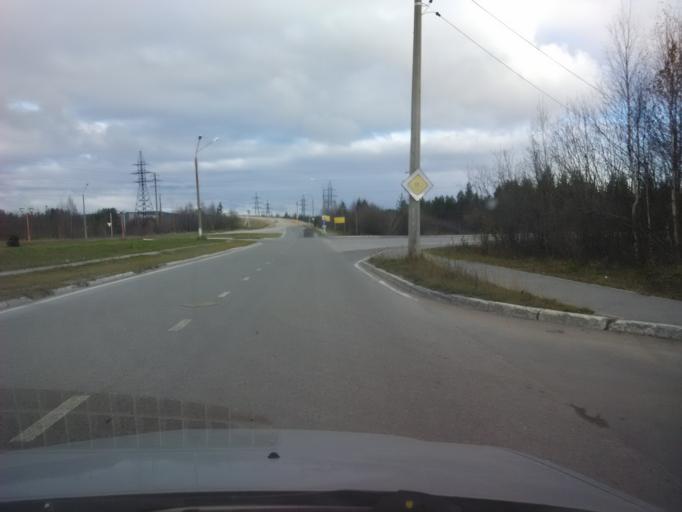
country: RU
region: Murmansk
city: Polyarnyye Zori
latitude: 67.3724
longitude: 32.5066
